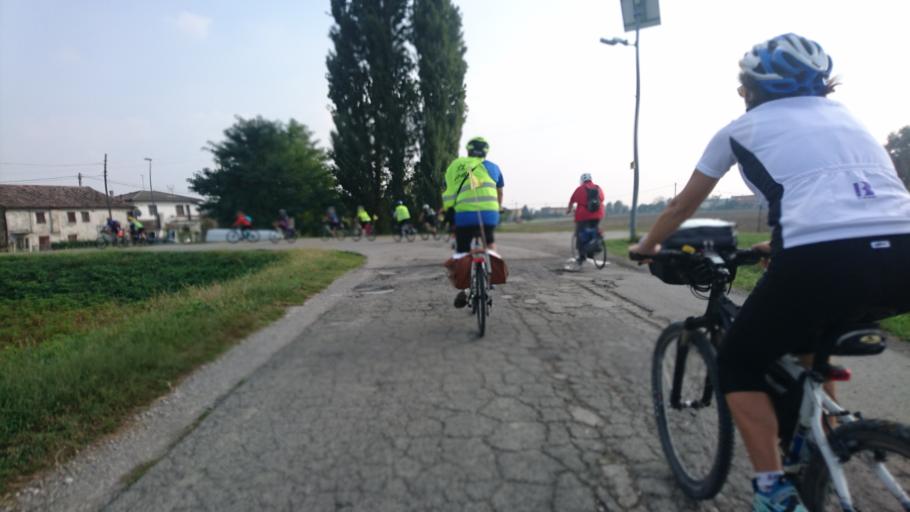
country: IT
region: Veneto
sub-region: Provincia di Rovigo
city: Arqua Polesine
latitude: 44.9952
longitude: 11.7285
